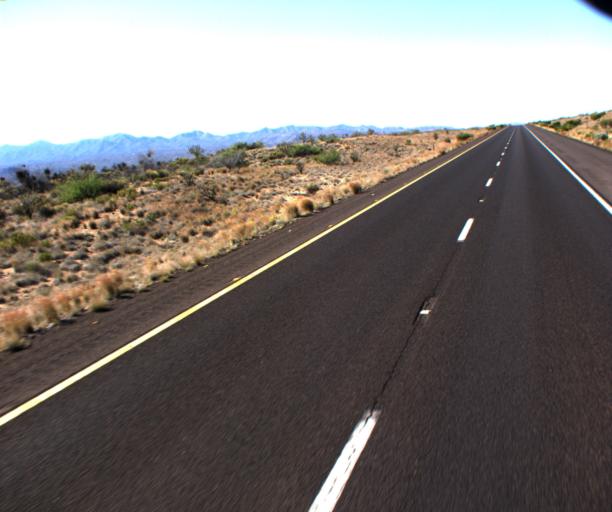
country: US
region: Arizona
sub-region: Mohave County
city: Kingman
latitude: 35.1161
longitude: -113.6668
